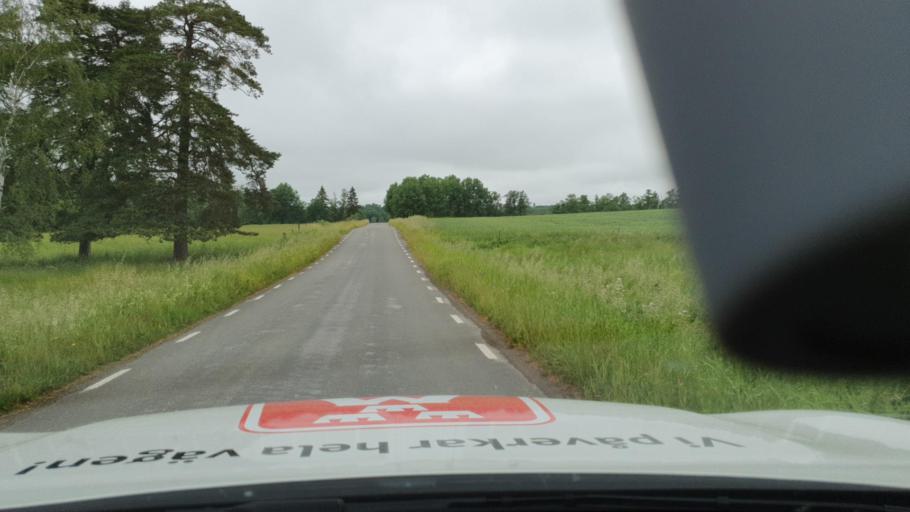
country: SE
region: Vaestra Goetaland
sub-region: Tidaholms Kommun
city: Olofstorp
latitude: 58.3910
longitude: 13.9916
